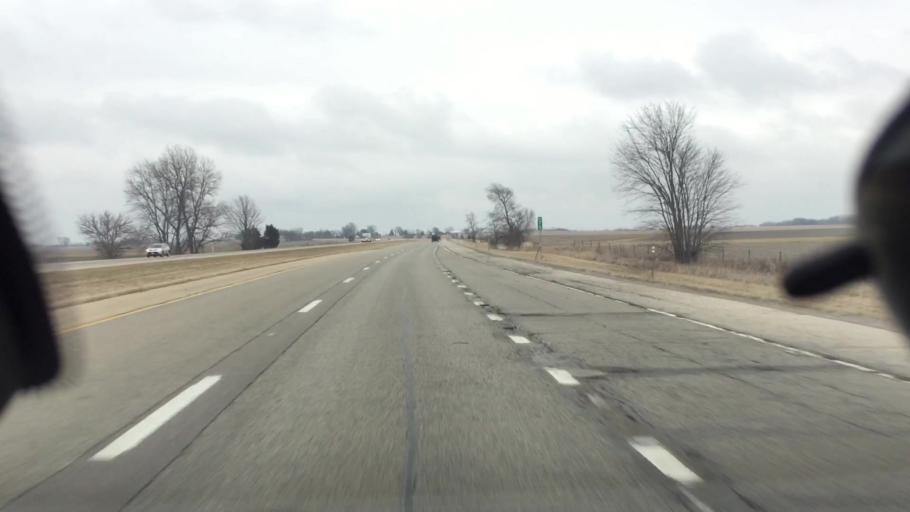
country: US
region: Illinois
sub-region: Peoria County
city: Elmwood
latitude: 40.8239
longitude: -89.8649
